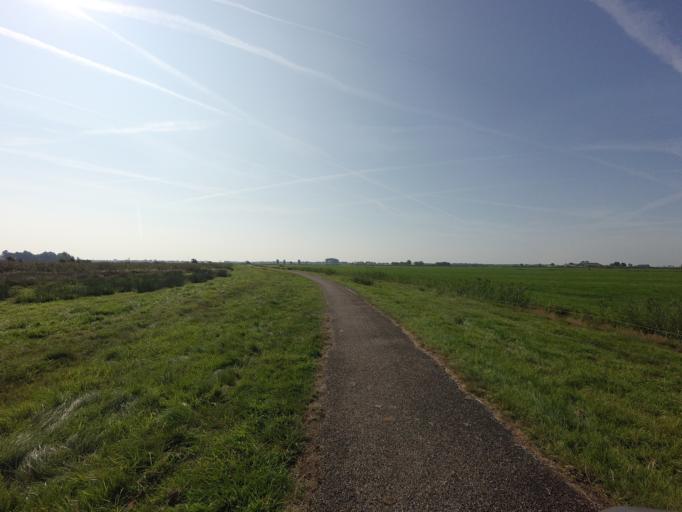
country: NL
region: Overijssel
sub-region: Gemeente Steenwijkerland
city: Oldemarkt
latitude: 52.8376
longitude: 5.9548
